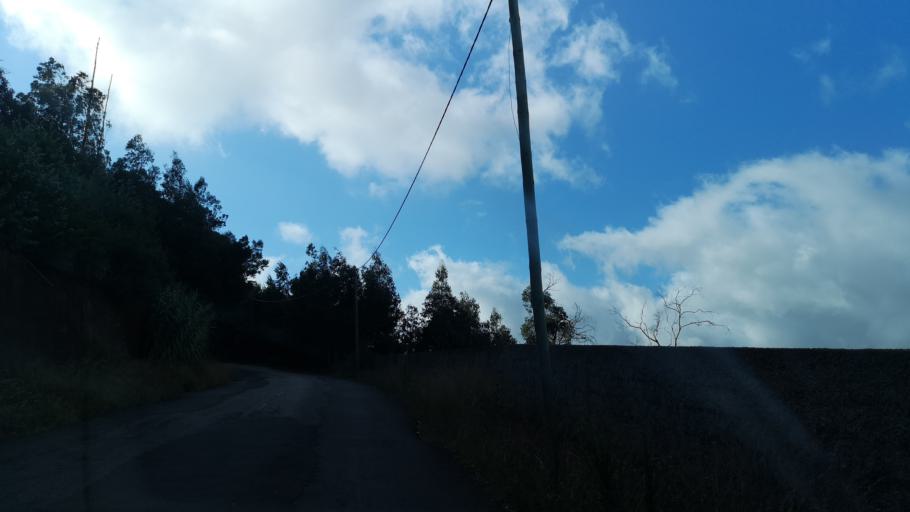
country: PT
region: Madeira
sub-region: Santa Cruz
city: Camacha
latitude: 32.6678
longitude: -16.8369
